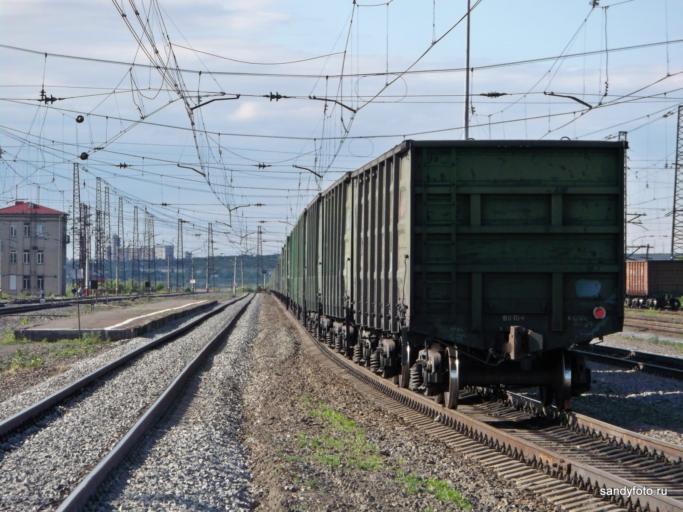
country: RU
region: Chelyabinsk
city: Troitsk
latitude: 54.0445
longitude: 61.6100
